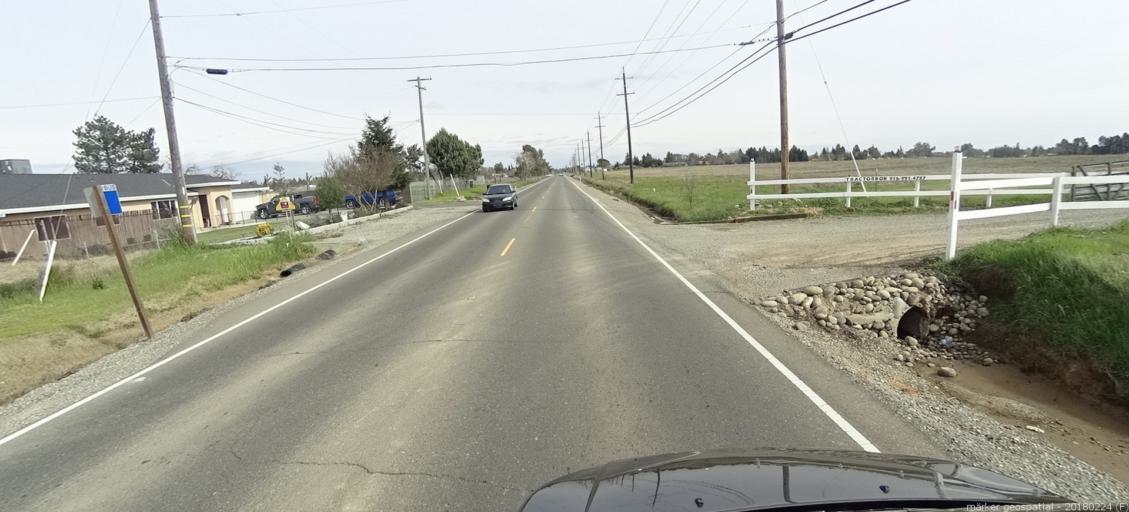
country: US
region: California
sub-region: Sacramento County
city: Rio Linda
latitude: 38.7144
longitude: -121.4264
